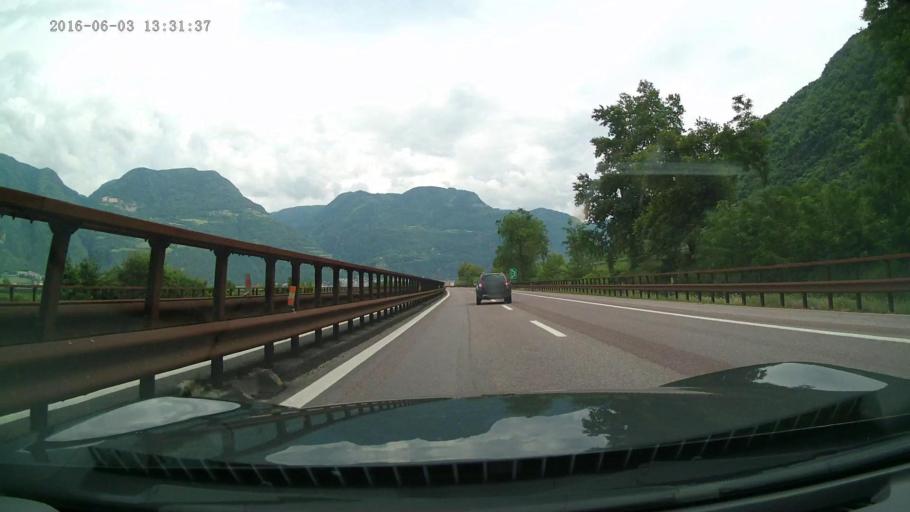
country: IT
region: Trentino-Alto Adige
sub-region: Bolzano
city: San Giacomo
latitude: 46.4489
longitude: 11.3091
